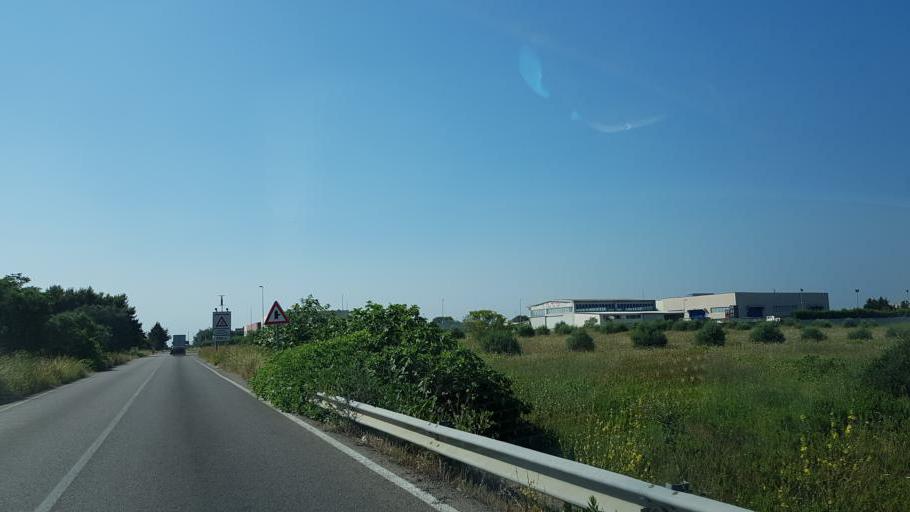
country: IT
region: Apulia
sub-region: Provincia di Lecce
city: Guagnano
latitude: 40.4158
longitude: 17.9559
